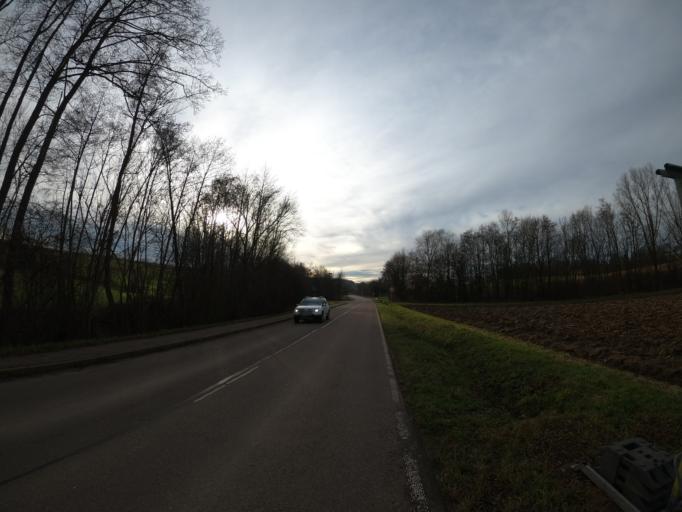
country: DE
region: Baden-Wuerttemberg
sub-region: Regierungsbezirk Stuttgart
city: Birenbach
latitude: 48.7271
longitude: 9.6737
